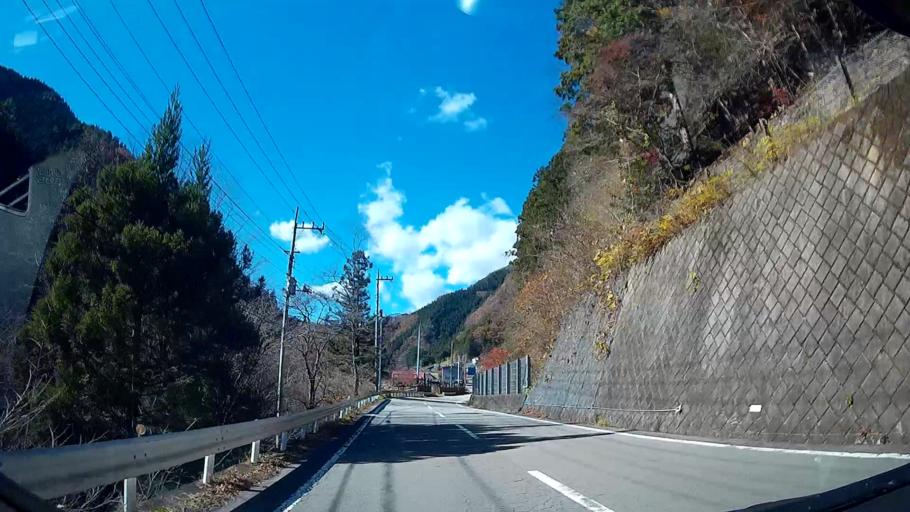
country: JP
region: Yamanashi
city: Otsuki
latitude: 35.7602
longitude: 138.9781
